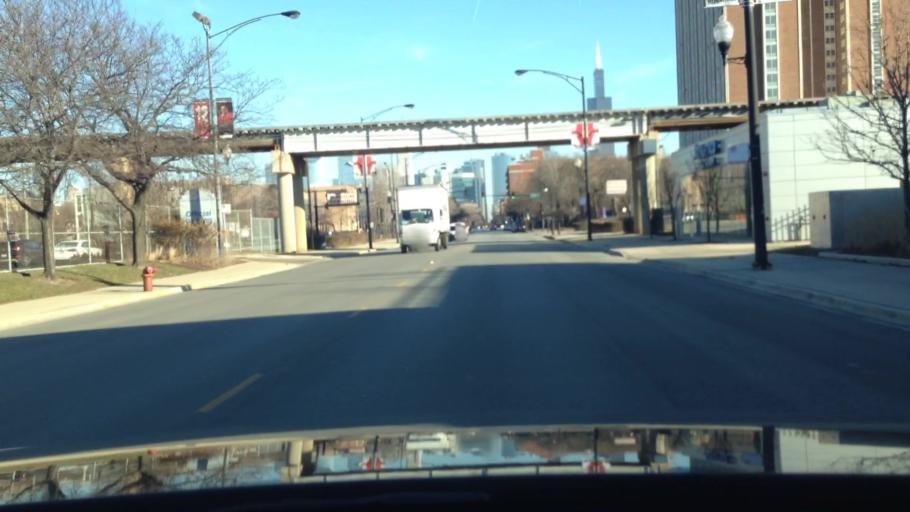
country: US
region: Illinois
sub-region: Cook County
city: Chicago
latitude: 41.8814
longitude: -87.6709
